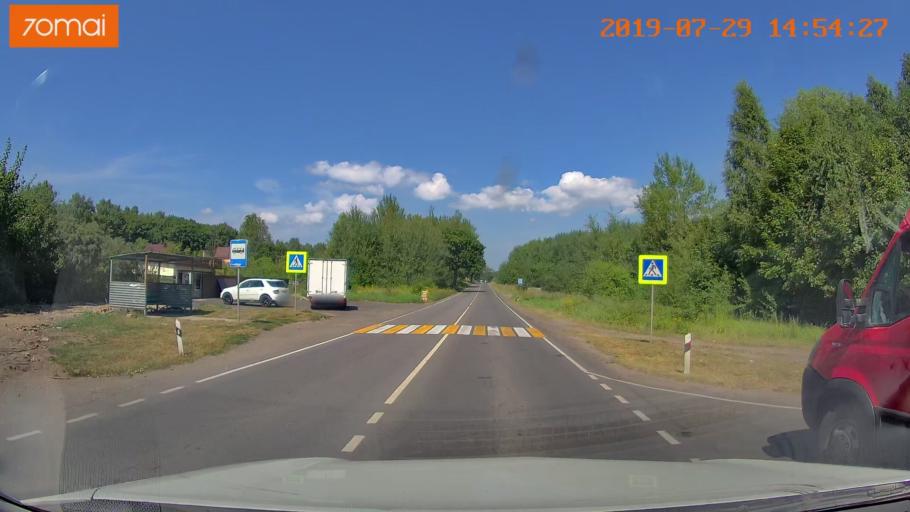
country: RU
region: Kaliningrad
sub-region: Gorod Kaliningrad
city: Baltiysk
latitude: 54.6741
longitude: 19.9248
